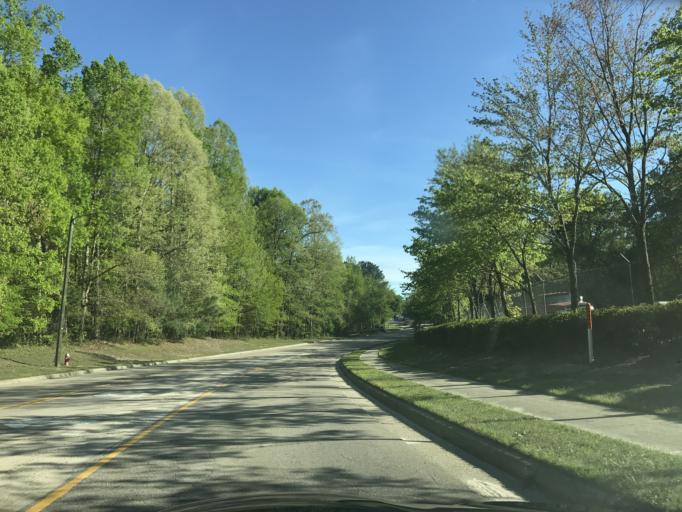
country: US
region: North Carolina
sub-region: Wake County
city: Knightdale
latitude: 35.8011
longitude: -78.5565
